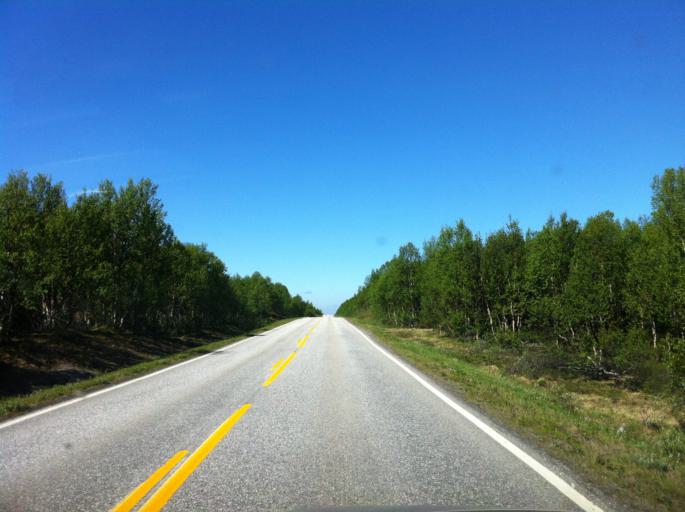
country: NO
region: Sor-Trondelag
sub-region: Tydal
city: Aas
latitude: 62.6368
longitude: 11.9887
